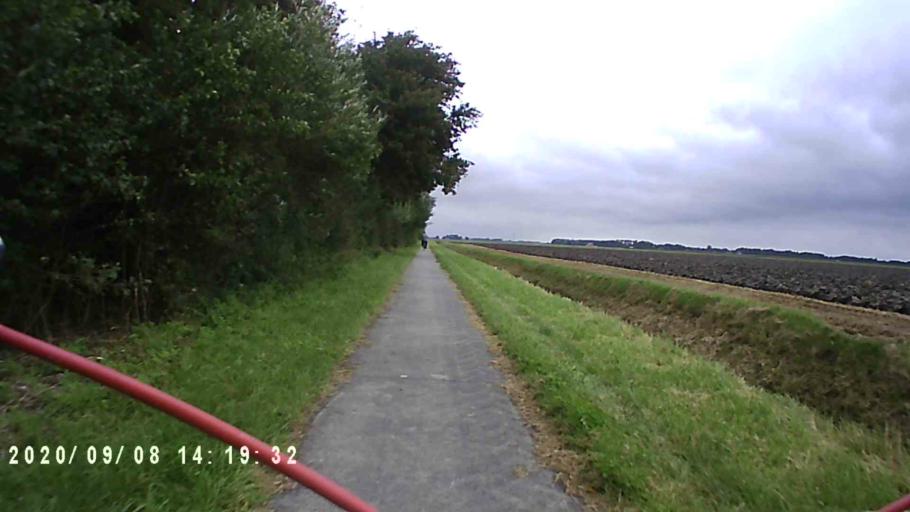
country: NL
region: Groningen
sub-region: Gemeente Slochteren
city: Slochteren
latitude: 53.2091
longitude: 6.8440
